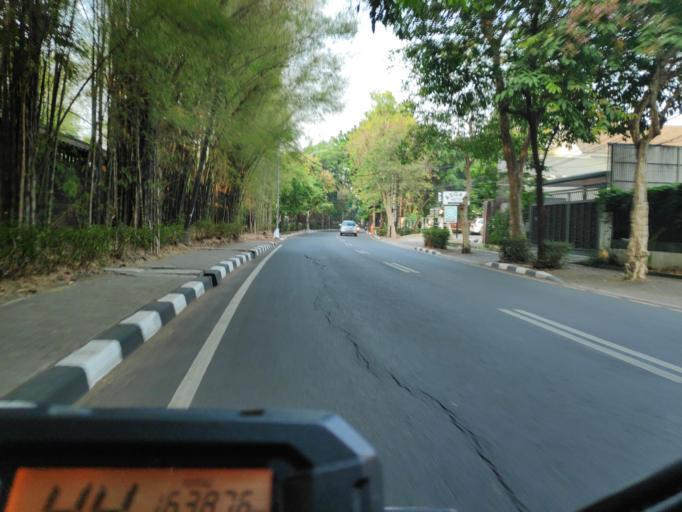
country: ID
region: Jakarta Raya
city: Jakarta
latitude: -6.2513
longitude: 106.8032
